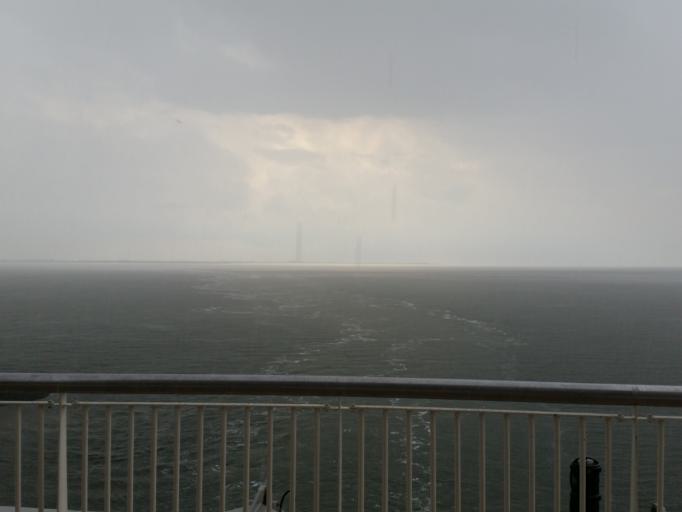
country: NL
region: North Holland
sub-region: Gemeente Den Helder
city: Den Helder
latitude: 52.9646
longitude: 4.7798
